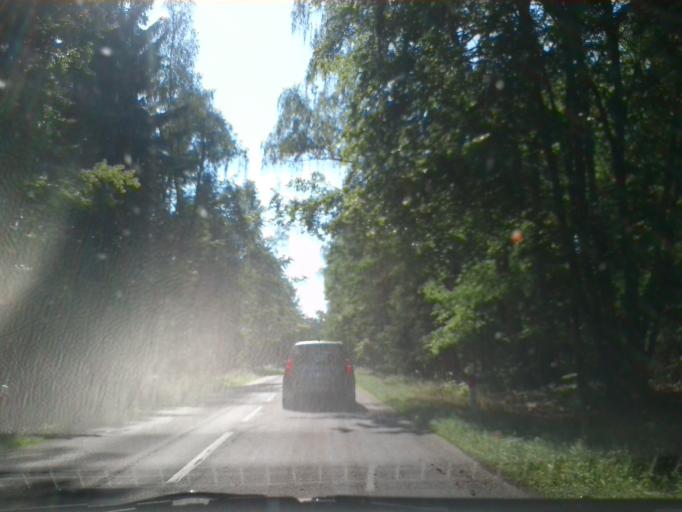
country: PL
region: West Pomeranian Voivodeship
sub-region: Powiat goleniowski
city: Stepnica
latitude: 53.6256
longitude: 14.6930
